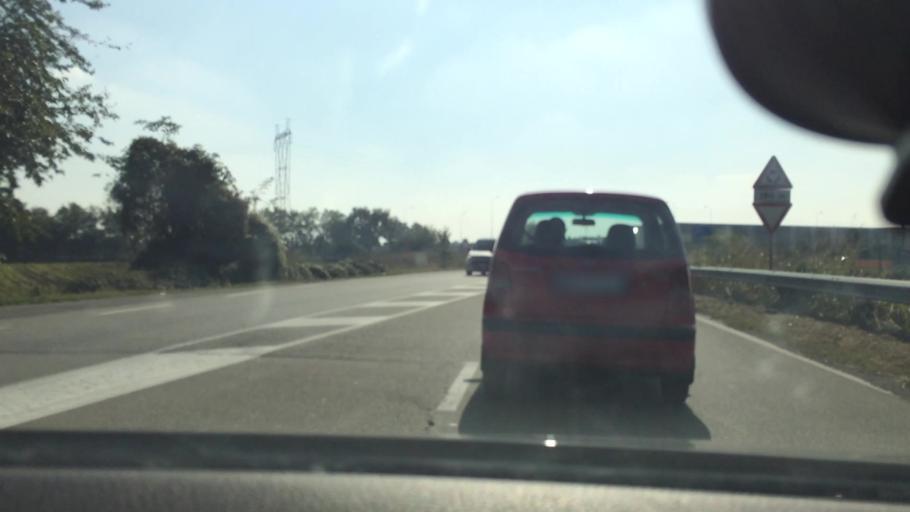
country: IT
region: Lombardy
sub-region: Citta metropolitana di Milano
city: Mesero
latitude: 45.5086
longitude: 8.8595
